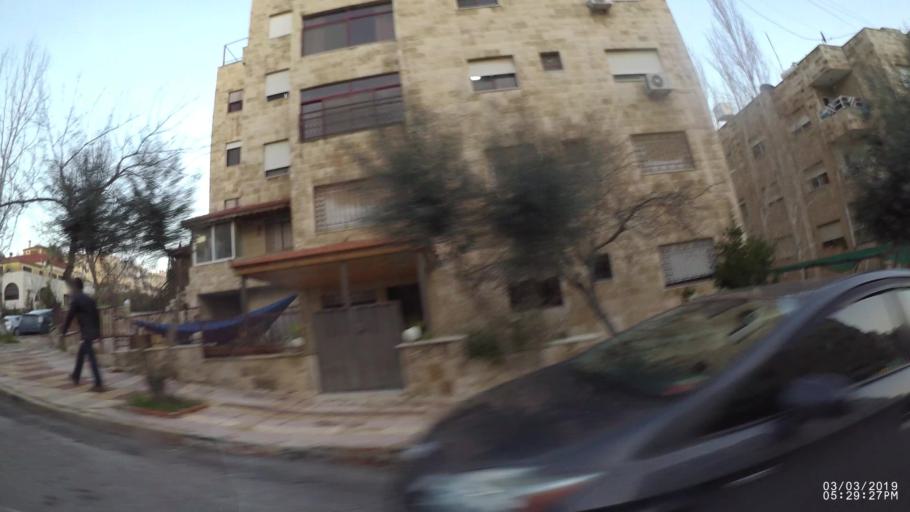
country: JO
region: Amman
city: Al Jubayhah
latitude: 31.9905
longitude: 35.8855
